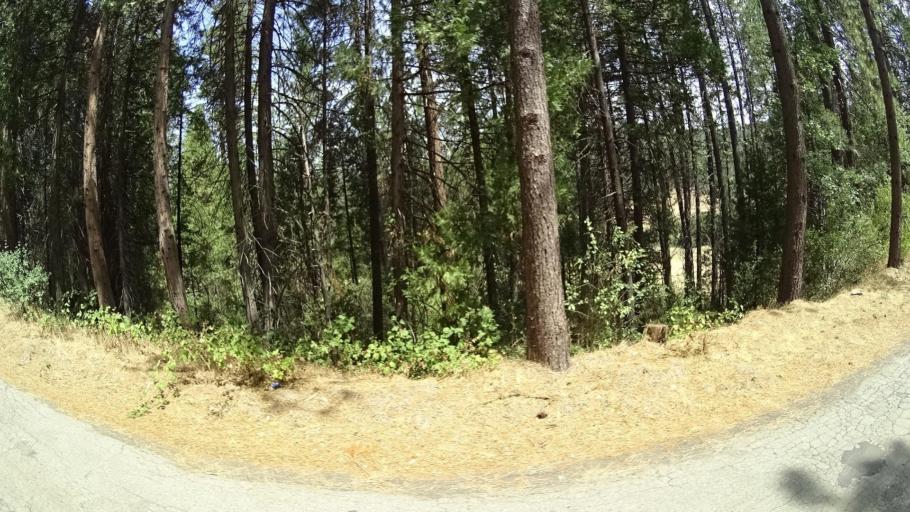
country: US
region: California
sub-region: Mariposa County
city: Midpines
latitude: 37.7532
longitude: -120.0612
